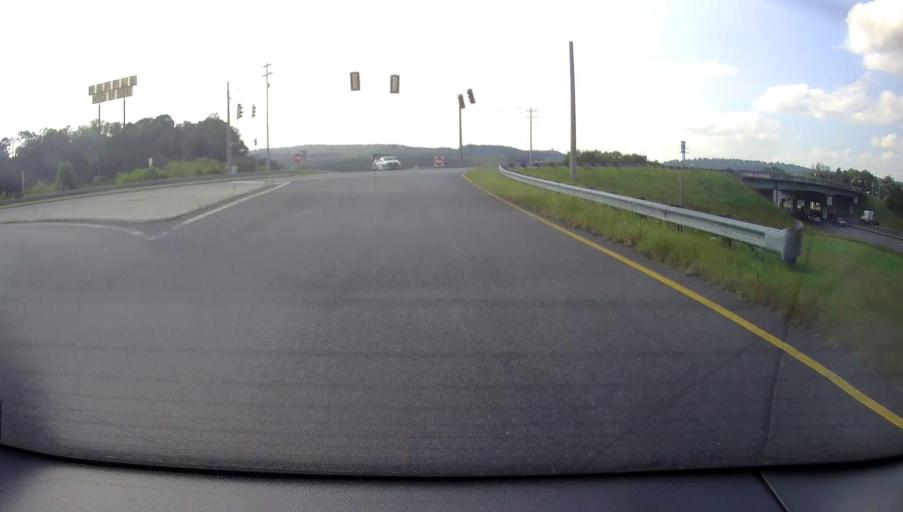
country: US
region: Georgia
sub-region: Catoosa County
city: Ringgold
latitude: 34.8911
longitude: -85.0735
